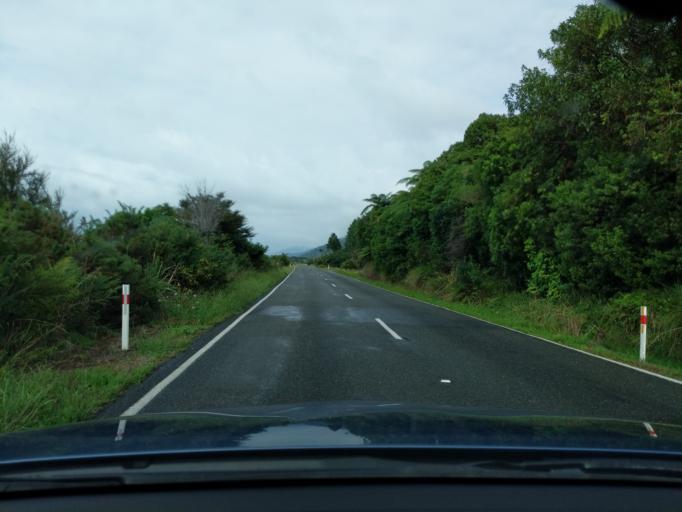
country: NZ
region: Tasman
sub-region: Tasman District
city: Takaka
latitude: -40.6415
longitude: 172.6647
